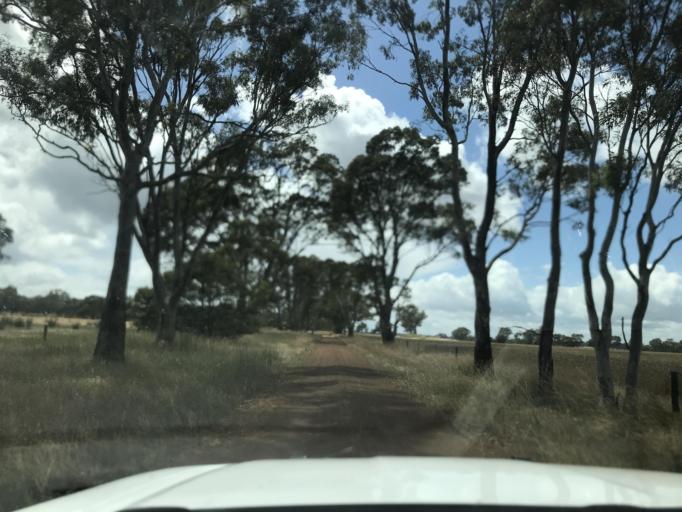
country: AU
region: South Australia
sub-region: Wattle Range
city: Penola
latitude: -37.1821
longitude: 141.4500
